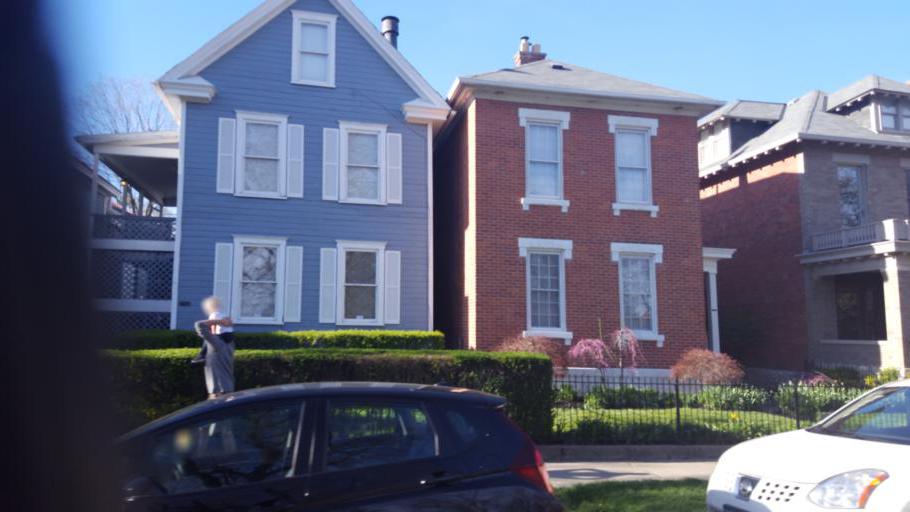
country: US
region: Ohio
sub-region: Franklin County
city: Columbus
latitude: 39.9436
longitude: -82.9913
